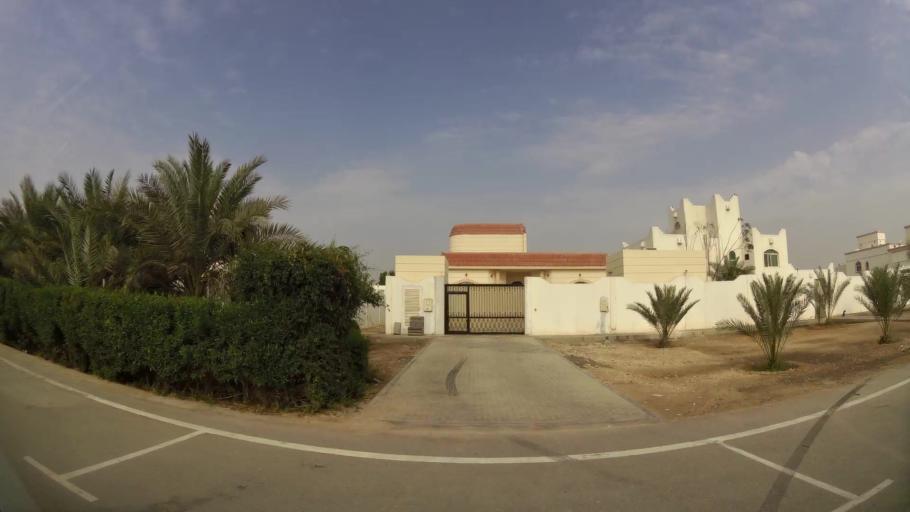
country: AE
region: Abu Dhabi
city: Abu Dhabi
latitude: 24.6567
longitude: 54.7568
